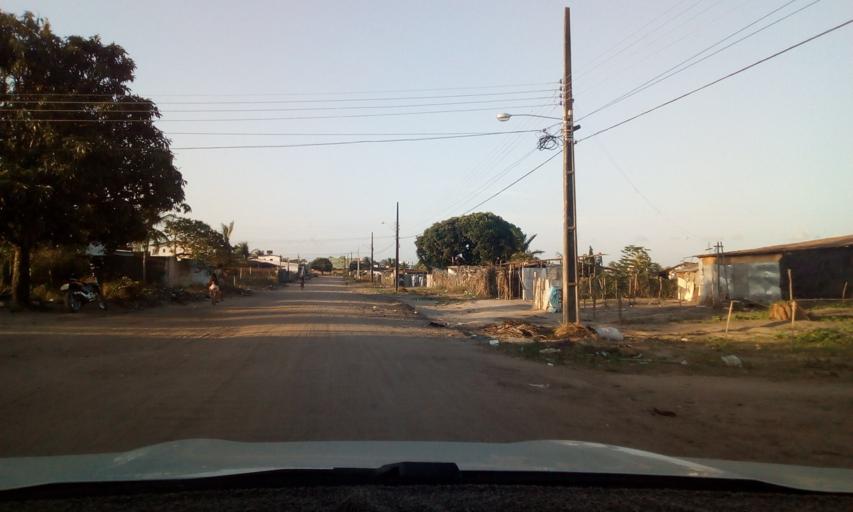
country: BR
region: Paraiba
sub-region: Bayeux
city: Bayeux
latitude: -7.1797
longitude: -34.9311
